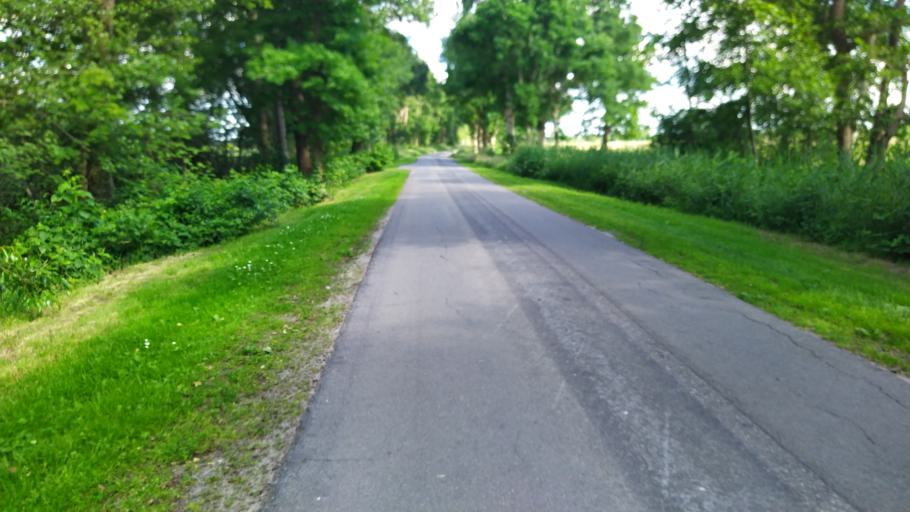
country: DE
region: Lower Saxony
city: Steinau
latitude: 53.6503
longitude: 8.9023
